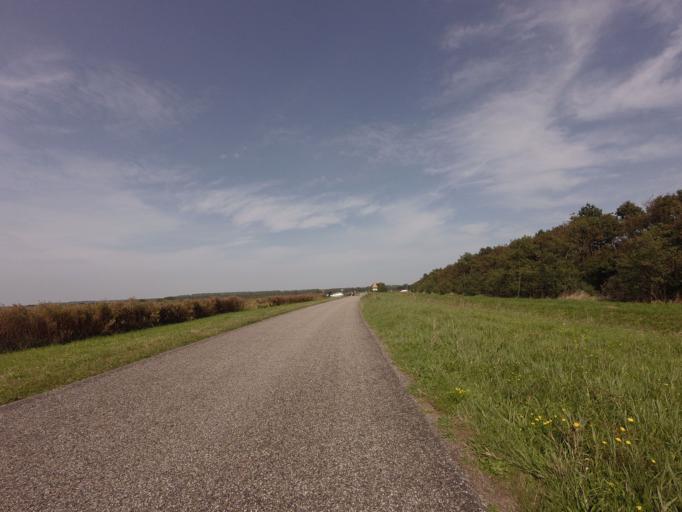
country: NL
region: Groningen
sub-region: Gemeente De Marne
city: Ulrum
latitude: 53.3594
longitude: 6.2611
